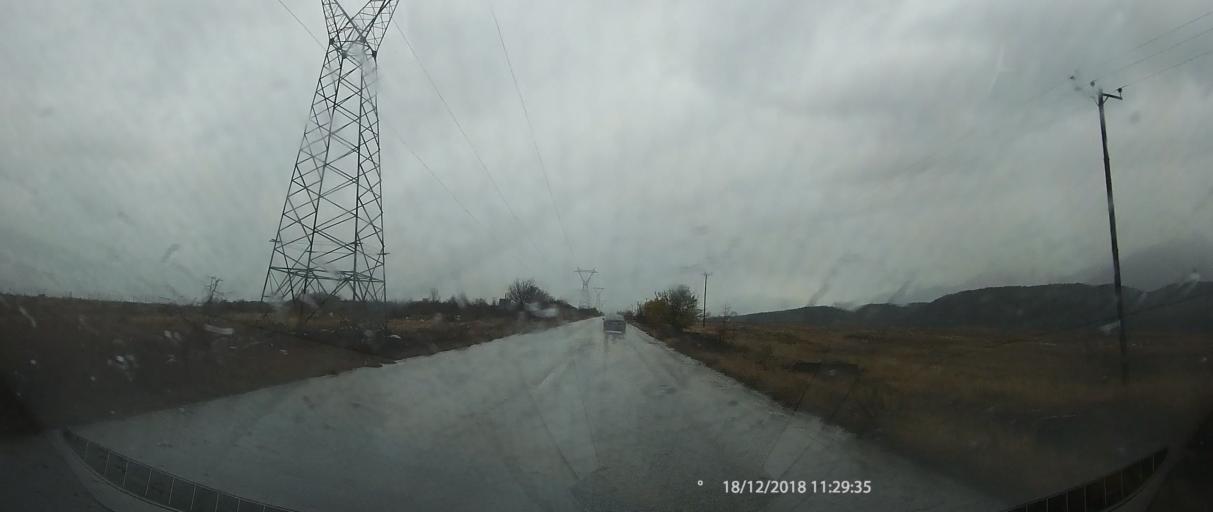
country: GR
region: Central Macedonia
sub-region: Nomos Pierias
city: Litochoro
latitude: 40.1343
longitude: 22.5214
